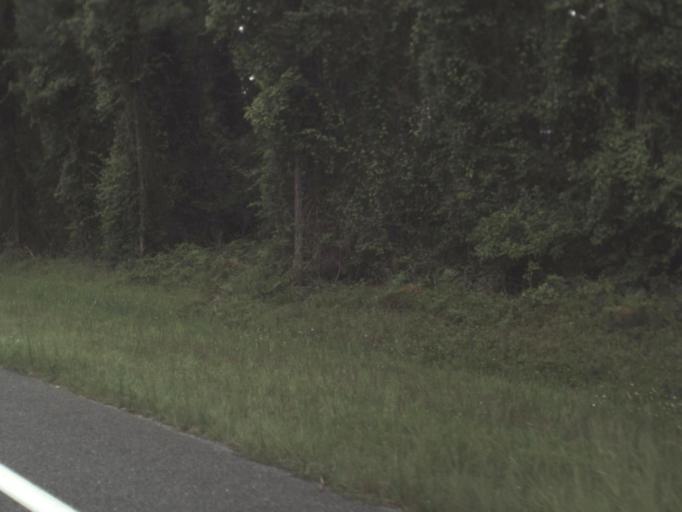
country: US
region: Florida
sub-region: Union County
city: Lake Butler
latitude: 30.0486
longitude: -82.4002
